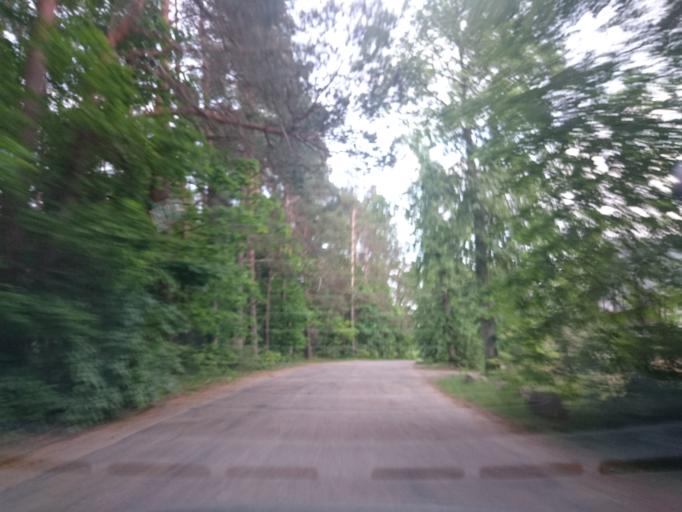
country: LV
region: Seja
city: Loja
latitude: 57.1223
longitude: 24.6467
